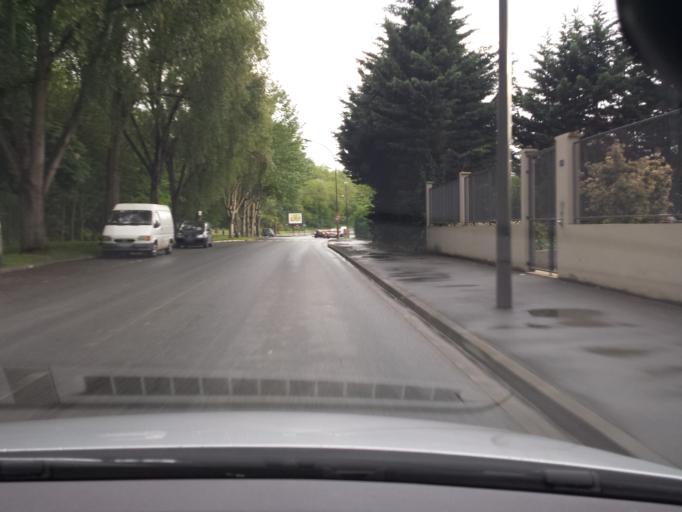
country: FR
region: Ile-de-France
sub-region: Departement de l'Essonne
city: Verrieres-le-Buisson
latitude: 48.7358
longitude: 2.2713
